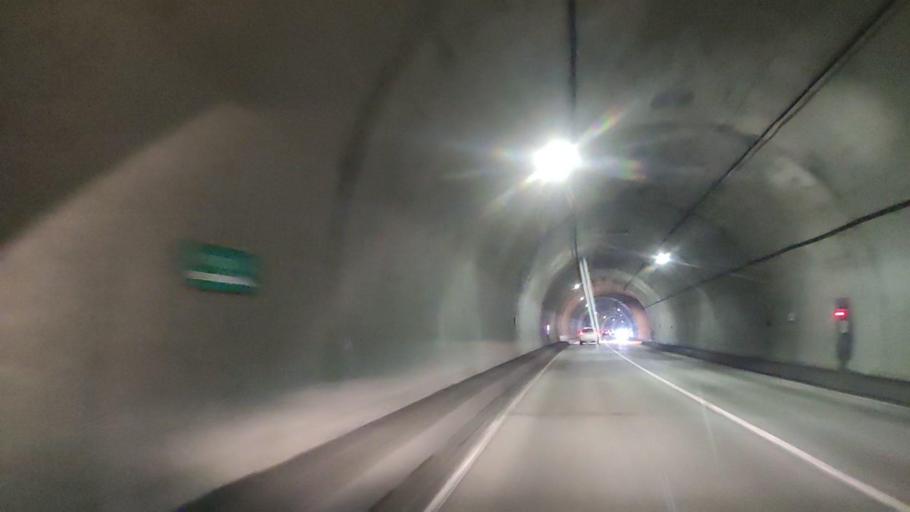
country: JP
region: Hokkaido
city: Ishikari
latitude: 43.5202
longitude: 141.3916
